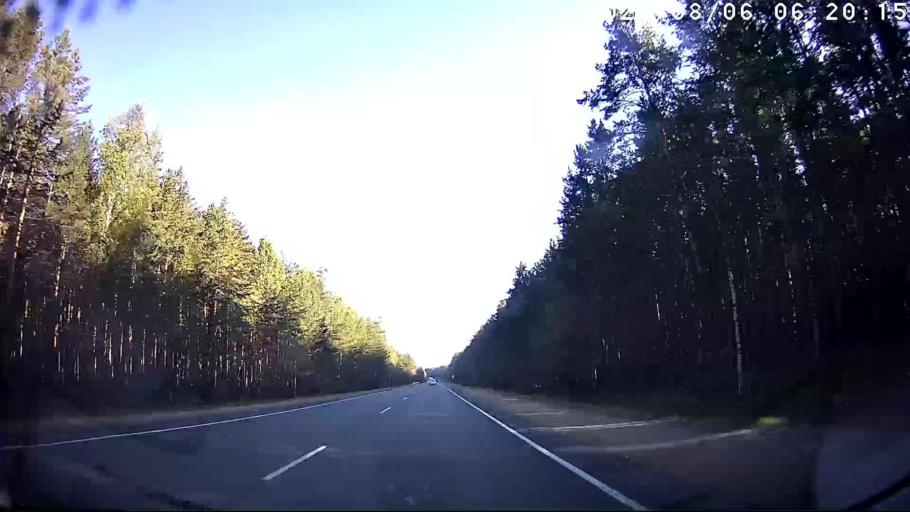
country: RU
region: Mariy-El
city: Pomary
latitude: 56.0519
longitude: 48.3742
